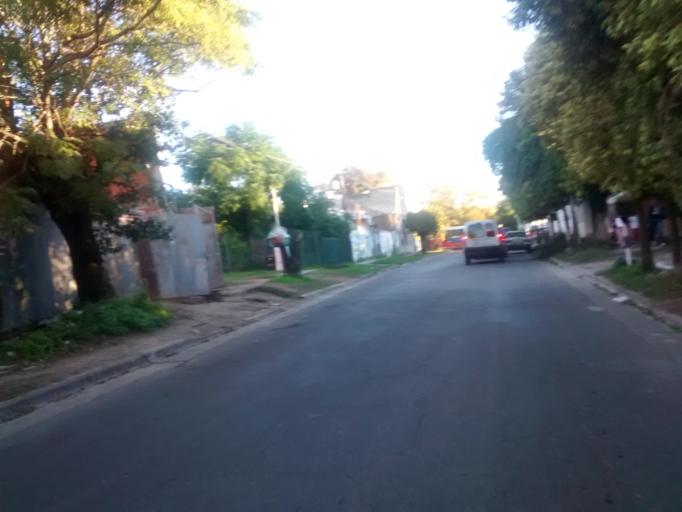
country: AR
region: Buenos Aires
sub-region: Partido de La Plata
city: La Plata
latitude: -34.9101
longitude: -57.9218
